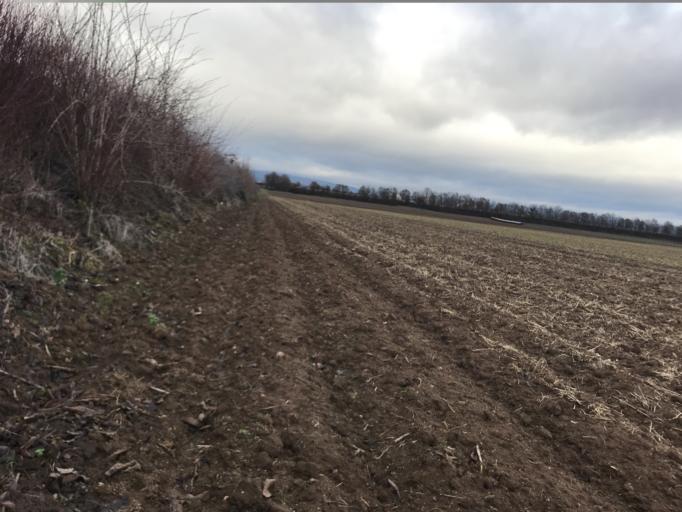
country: DE
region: Rheinland-Pfalz
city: Klein-Winternheim
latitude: 49.9856
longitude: 8.2101
